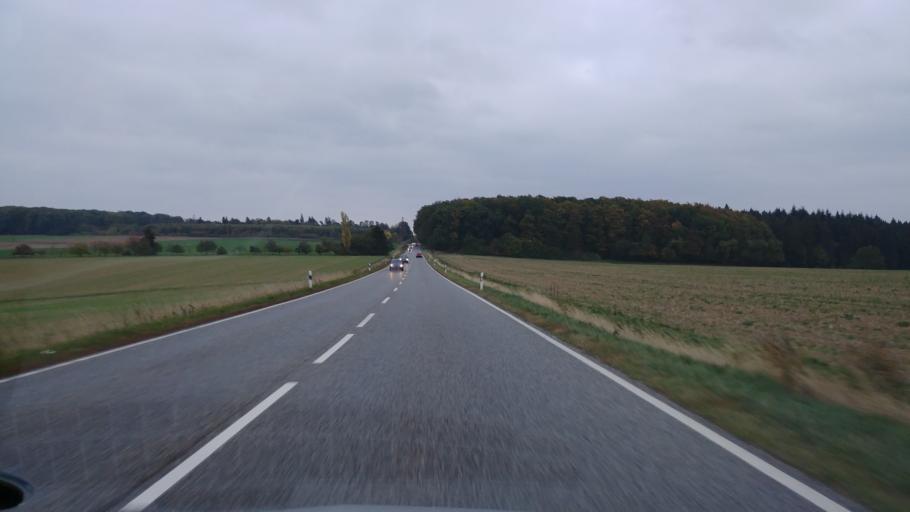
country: DE
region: Hesse
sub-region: Regierungsbezirk Darmstadt
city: Idstein
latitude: 50.2429
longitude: 8.1888
